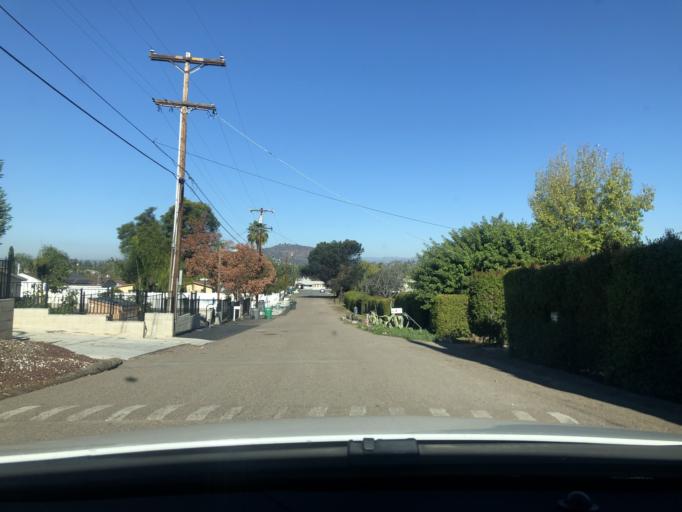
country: US
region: California
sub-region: San Diego County
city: Bostonia
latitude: 32.7853
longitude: -116.9395
